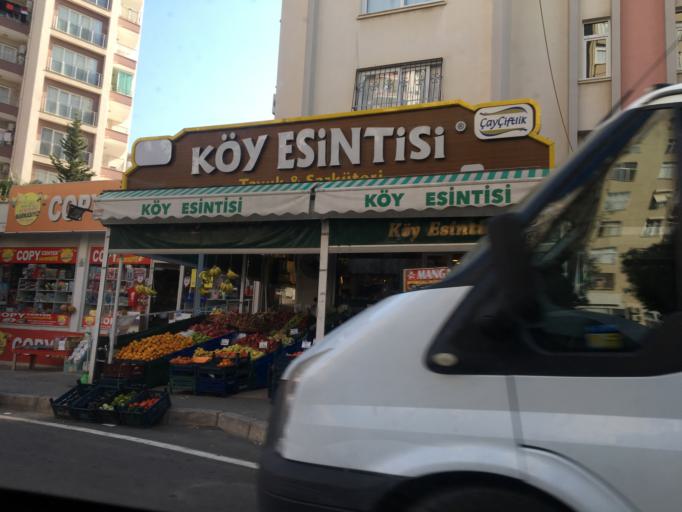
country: TR
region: Adana
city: Seyhan
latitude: 37.0361
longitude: 35.2820
